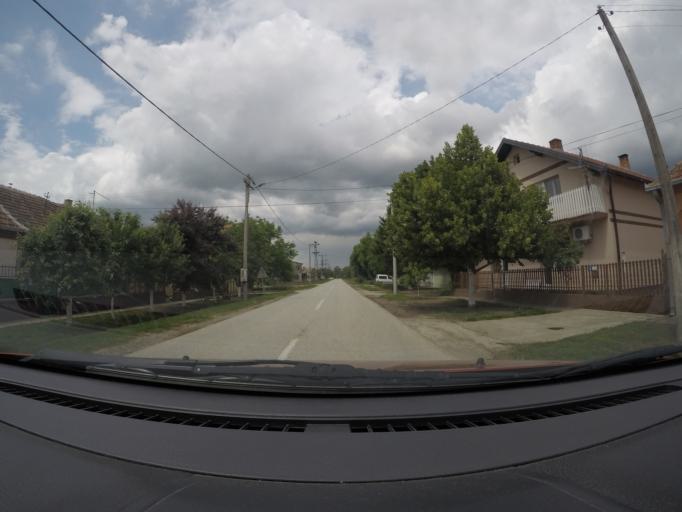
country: RS
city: Centa
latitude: 45.1144
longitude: 20.3895
